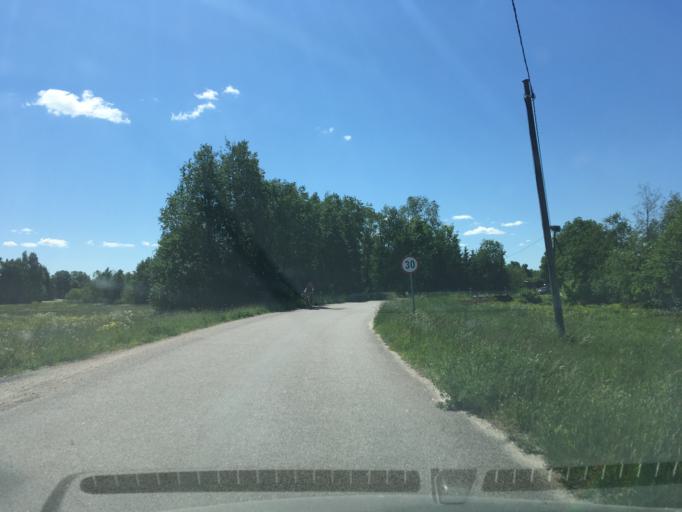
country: EE
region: Harju
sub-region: Rae vald
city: Vaida
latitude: 59.1712
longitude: 25.1246
